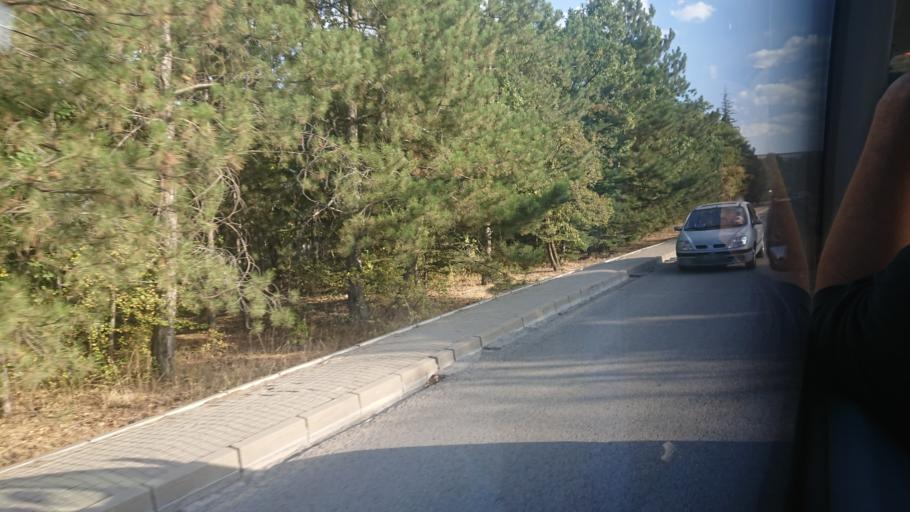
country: TR
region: Ankara
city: Ankara
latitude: 39.8917
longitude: 32.7840
